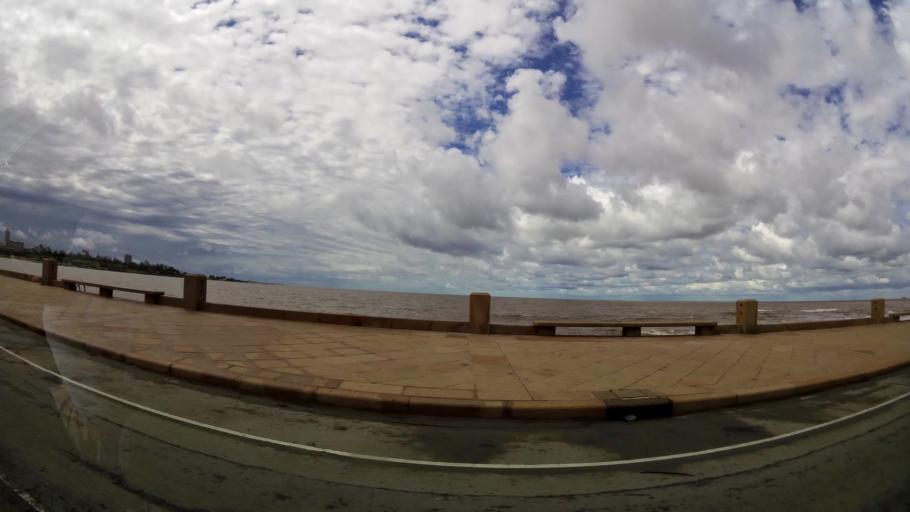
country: UY
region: Montevideo
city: Montevideo
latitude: -34.9154
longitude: -56.1827
